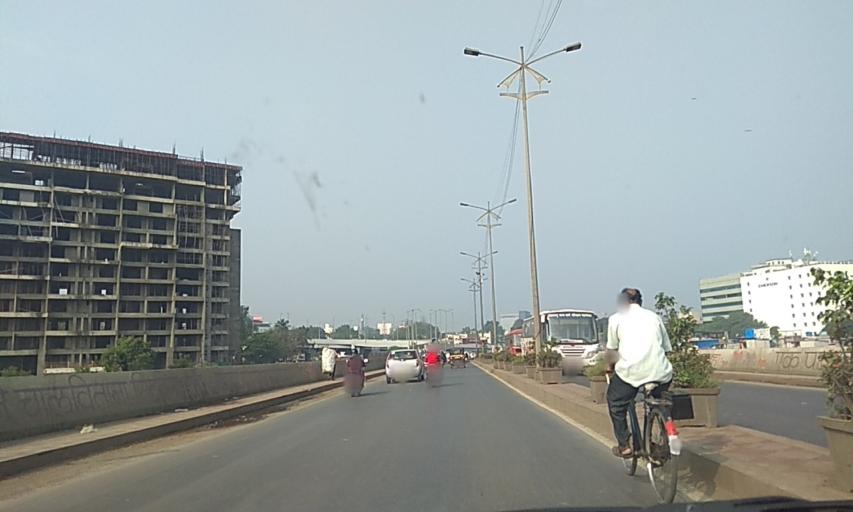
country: IN
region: Maharashtra
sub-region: Pune Division
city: Shivaji Nagar
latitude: 18.5325
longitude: 73.8560
